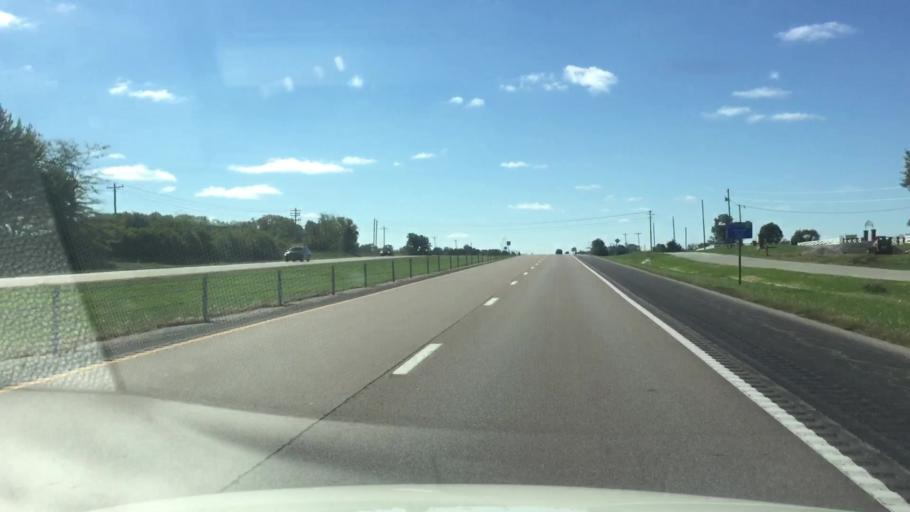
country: US
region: Missouri
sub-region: Boone County
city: Ashland
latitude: 38.8009
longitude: -92.2516
